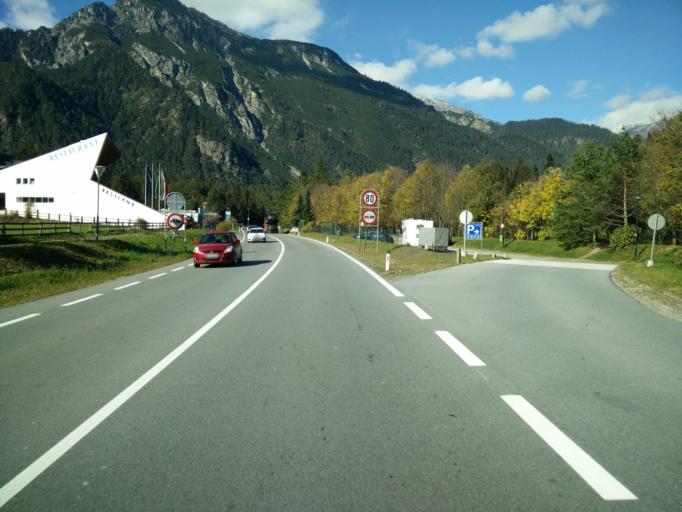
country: AT
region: Tyrol
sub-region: Politischer Bezirk Imst
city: Nassereith
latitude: 47.3261
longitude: 10.8219
